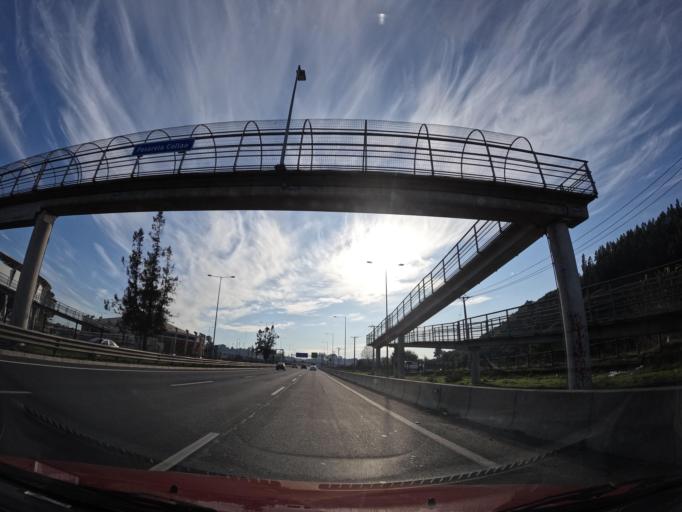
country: CL
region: Biobio
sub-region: Provincia de Concepcion
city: Concepcion
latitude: -36.8140
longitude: -73.0221
